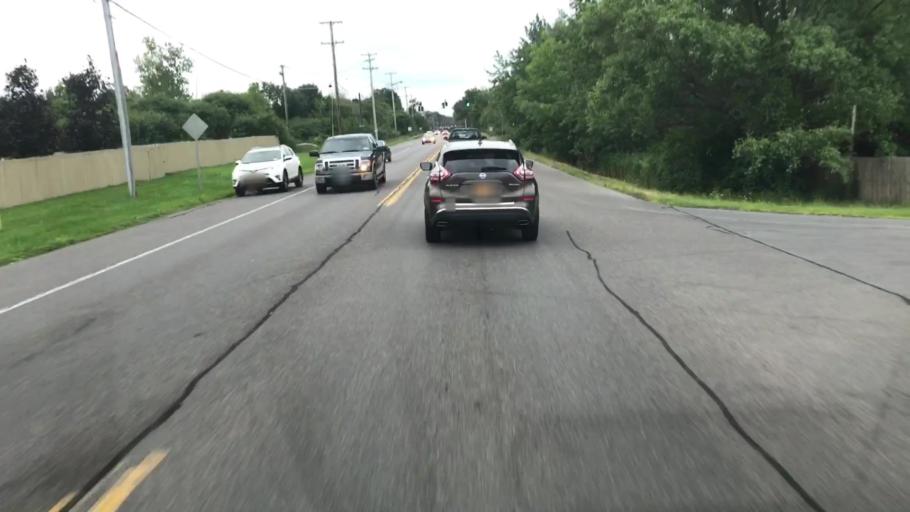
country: US
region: New York
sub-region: Onondaga County
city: North Syracuse
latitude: 43.1406
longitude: -76.1764
